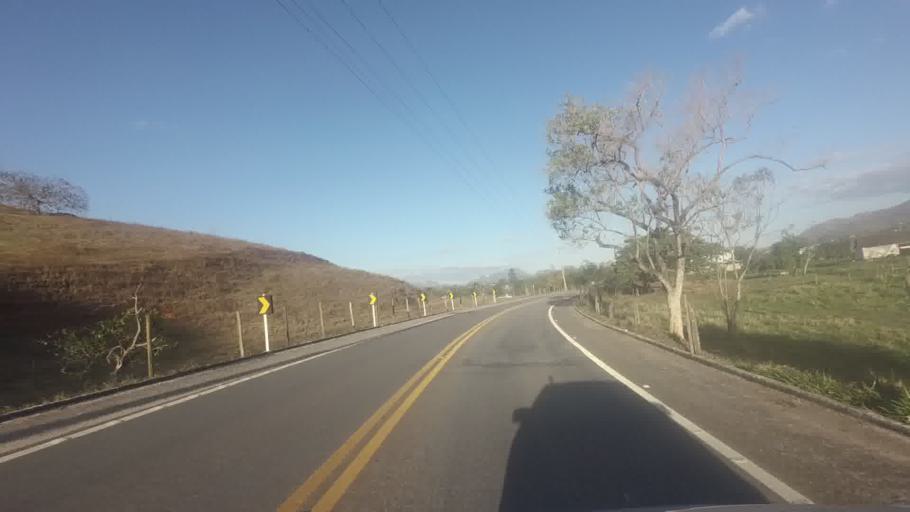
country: BR
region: Espirito Santo
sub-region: Cachoeiro De Itapemirim
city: Cachoeiro de Itapemirim
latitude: -20.8260
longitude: -41.1868
